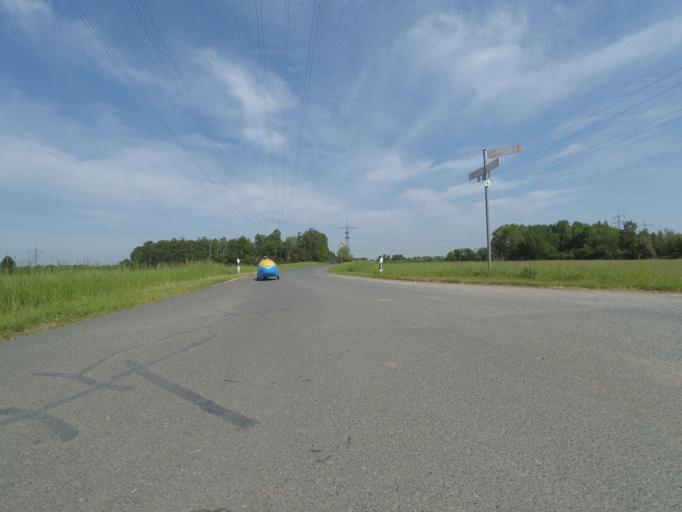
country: DE
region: Lower Saxony
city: Lehrte
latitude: 52.3985
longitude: 9.9959
